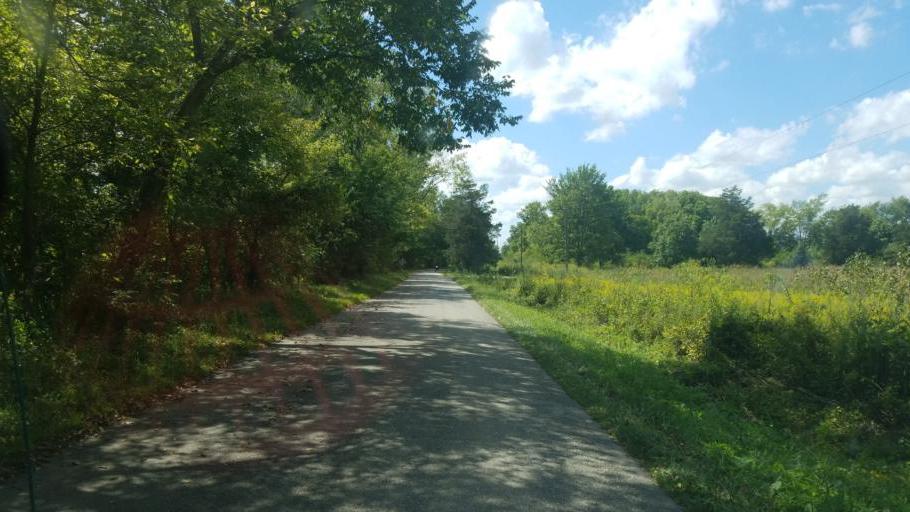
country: US
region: Ohio
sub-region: Marion County
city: Prospect
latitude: 40.3728
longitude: -83.2088
